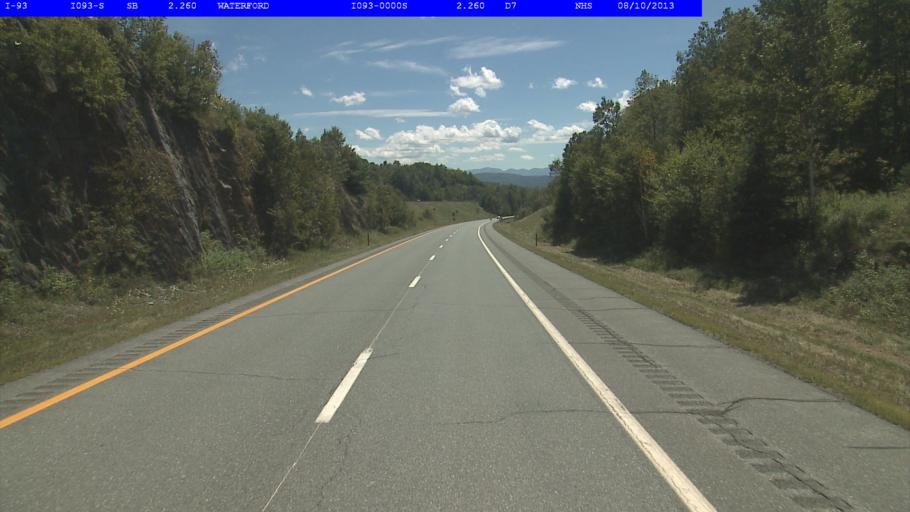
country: US
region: Vermont
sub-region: Caledonia County
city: Saint Johnsbury
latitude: 44.3733
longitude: -71.9086
